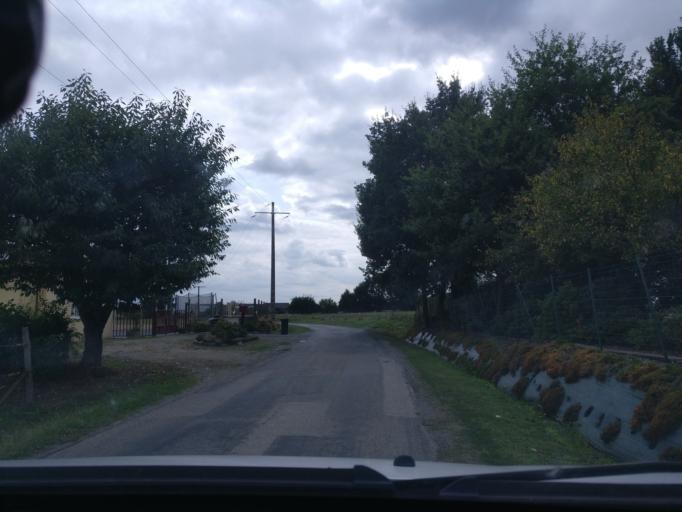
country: FR
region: Brittany
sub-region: Departement d'Ille-et-Vilaine
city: Nouvoitou
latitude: 48.0758
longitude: -1.5345
